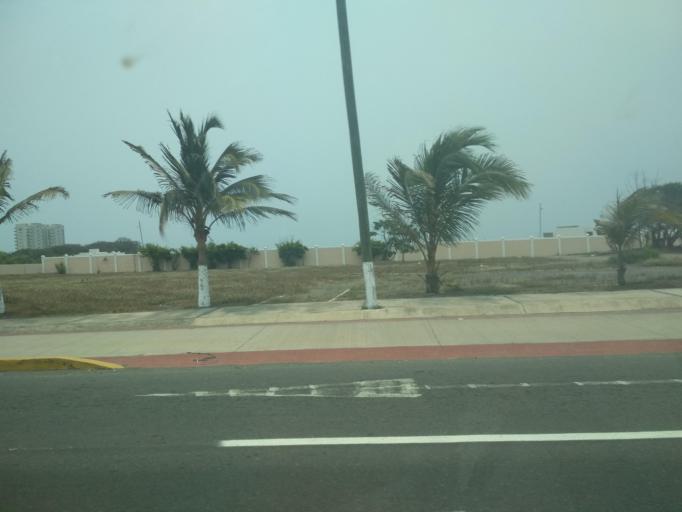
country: MX
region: Veracruz
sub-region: Alvarado
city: Playa de la Libertad
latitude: 19.0698
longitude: -96.0835
